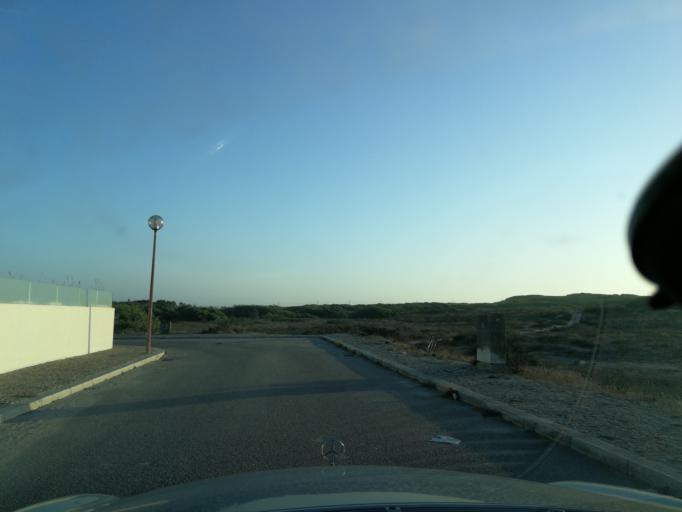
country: PT
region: Aveiro
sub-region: Murtosa
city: Murtosa
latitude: 40.7570
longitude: -8.7112
